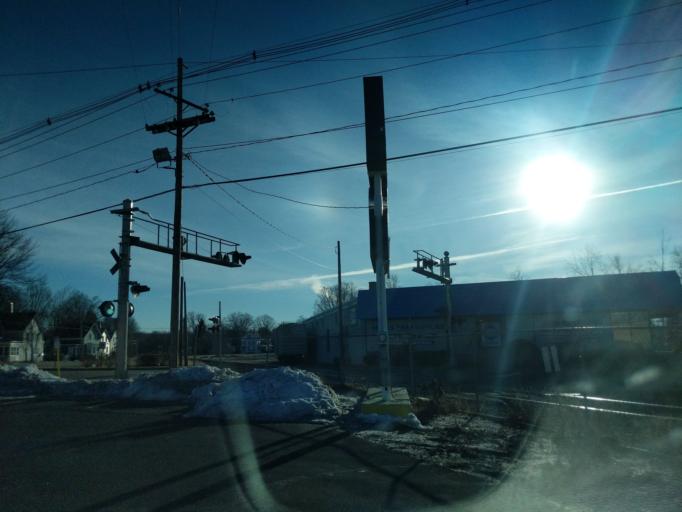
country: US
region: New Hampshire
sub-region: Strafford County
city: Rochester
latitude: 43.3050
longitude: -70.9722
